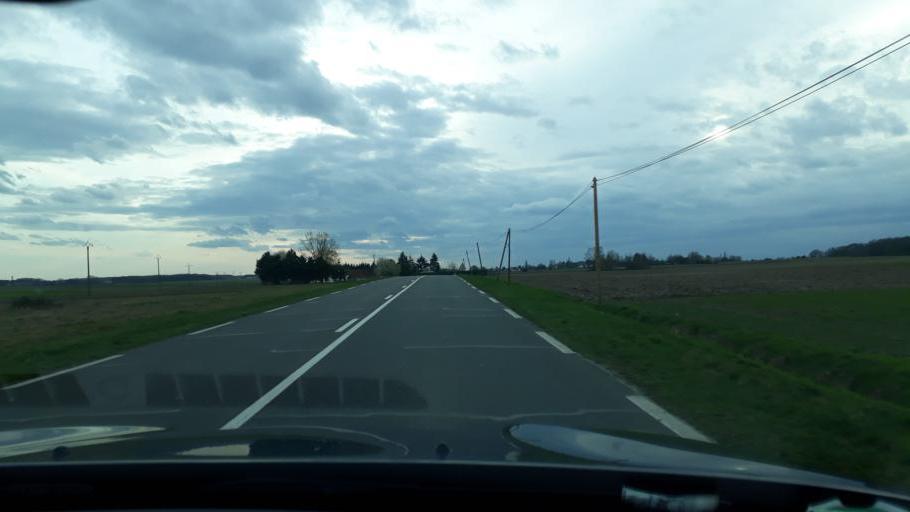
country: FR
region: Centre
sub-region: Departement du Loiret
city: Loury
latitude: 48.0147
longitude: 2.1085
